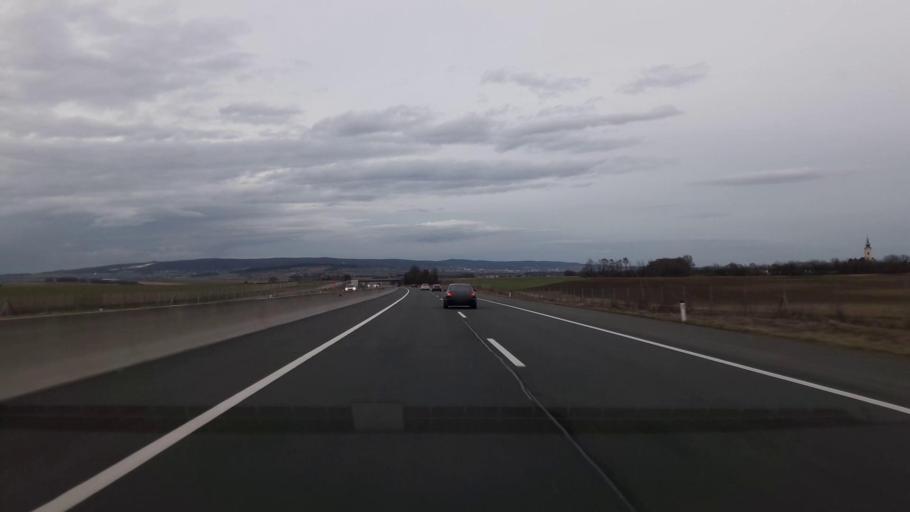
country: AT
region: Burgenland
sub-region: Politischer Bezirk Mattersburg
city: Pottelsdorf
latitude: 47.7698
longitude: 16.4276
